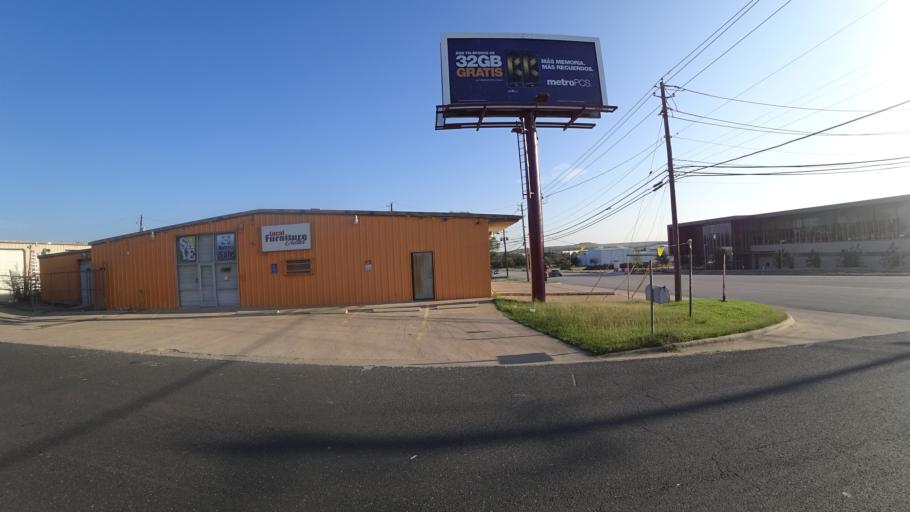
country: US
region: Texas
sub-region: Travis County
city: Austin
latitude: 30.3212
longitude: -97.6600
